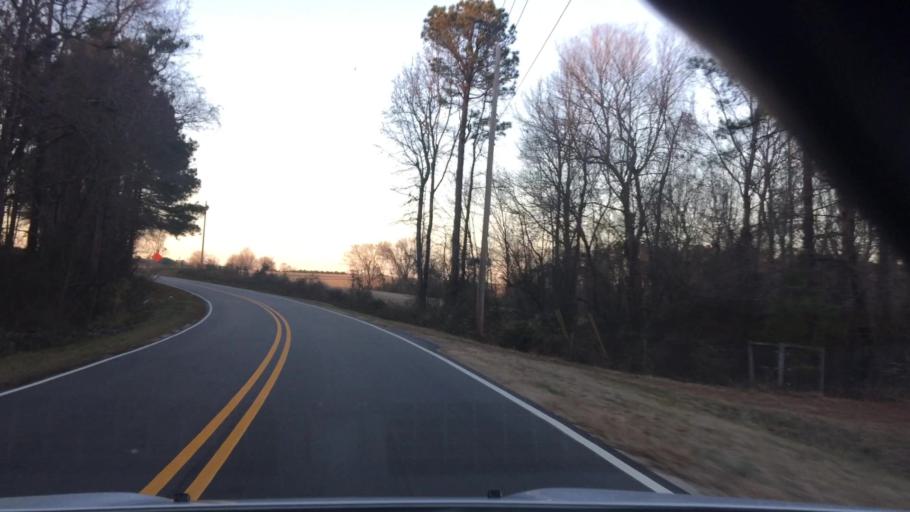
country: US
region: North Carolina
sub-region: Wake County
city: Rolesville
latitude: 35.9537
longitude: -78.4107
